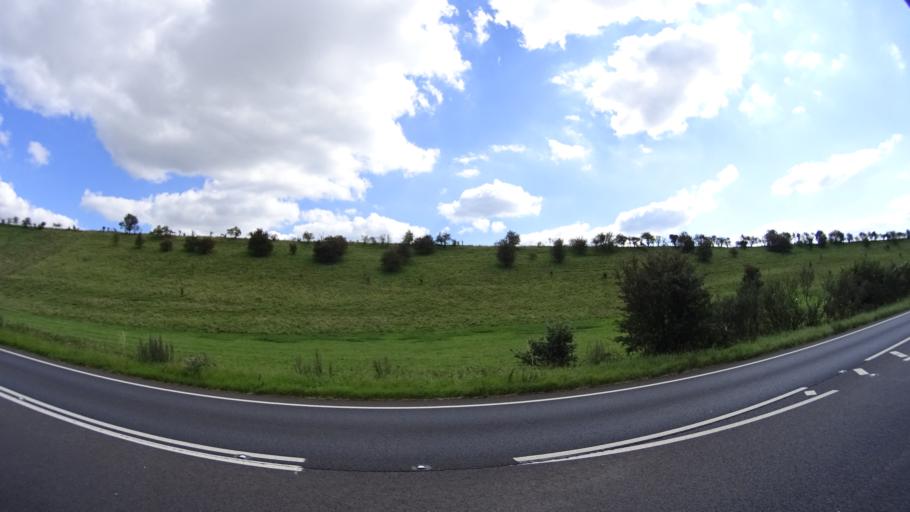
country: GB
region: England
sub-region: Wiltshire
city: Mere
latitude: 51.0974
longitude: -2.2252
